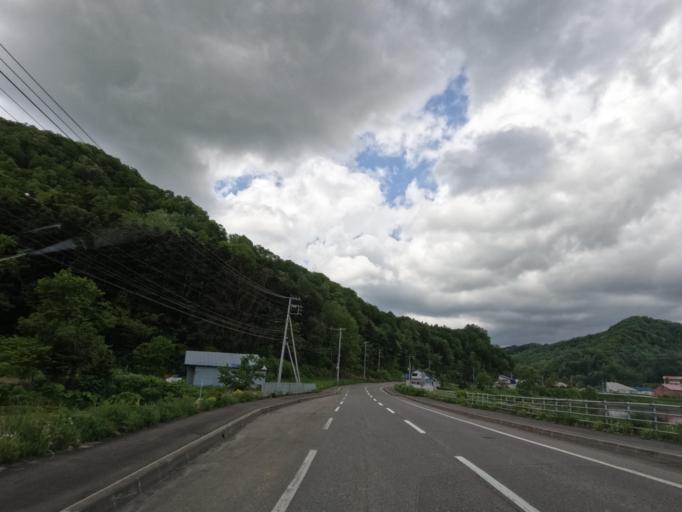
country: JP
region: Hokkaido
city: Takikawa
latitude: 43.5906
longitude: 141.7318
